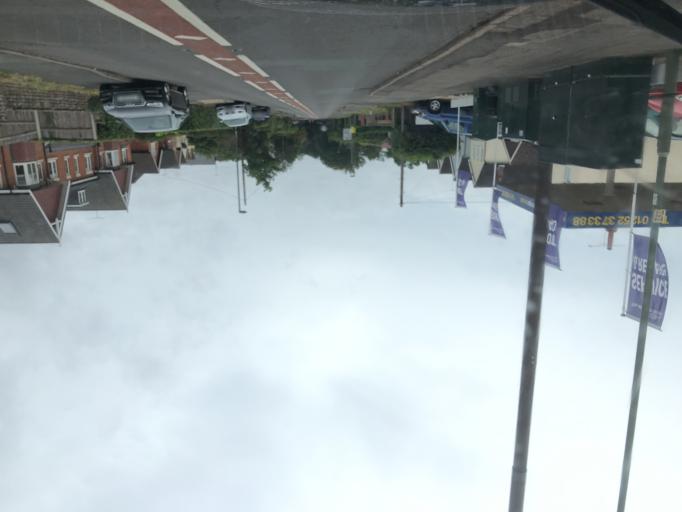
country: GB
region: England
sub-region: Hampshire
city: Farnborough
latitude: 51.2906
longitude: -0.7259
